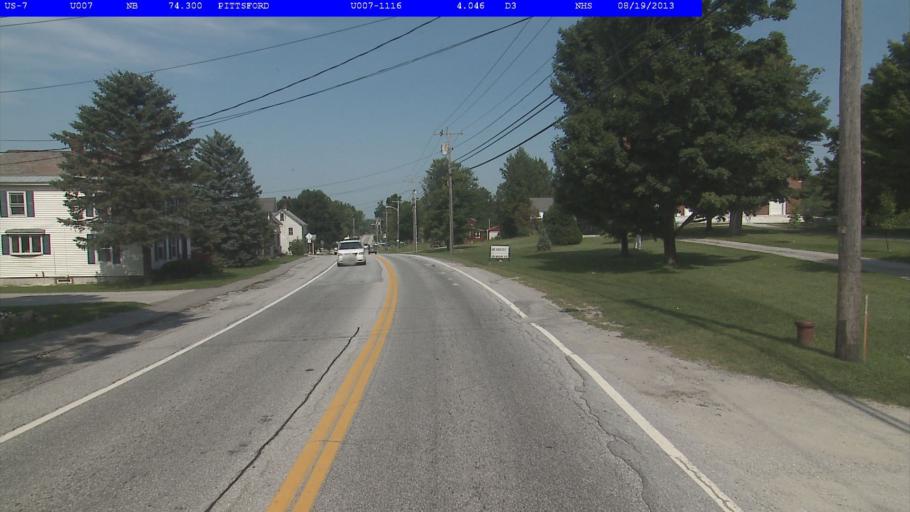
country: US
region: Vermont
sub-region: Rutland County
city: Brandon
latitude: 43.7076
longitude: -73.0287
